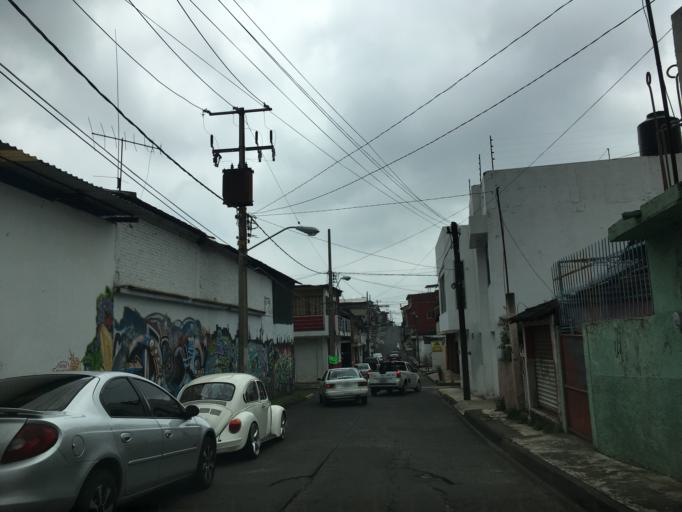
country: MX
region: Michoacan
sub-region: Uruapan
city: Uruapan
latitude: 19.4286
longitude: -102.0626
